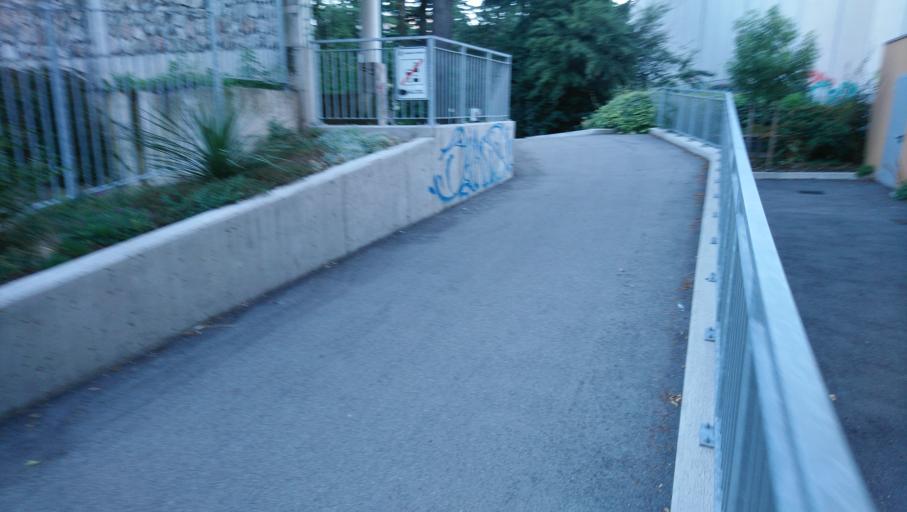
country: IT
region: Trentino-Alto Adige
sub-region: Provincia di Trento
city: Trento
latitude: 46.0641
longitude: 11.1255
